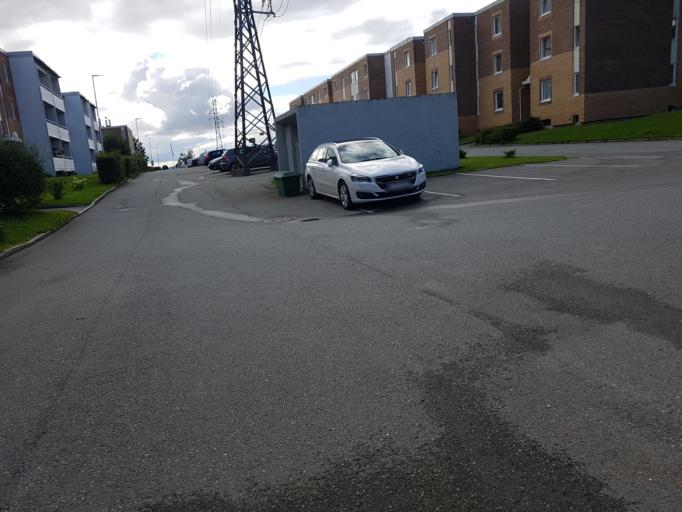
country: NO
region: Sor-Trondelag
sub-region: Trondheim
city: Trondheim
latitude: 63.4089
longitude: 10.4350
